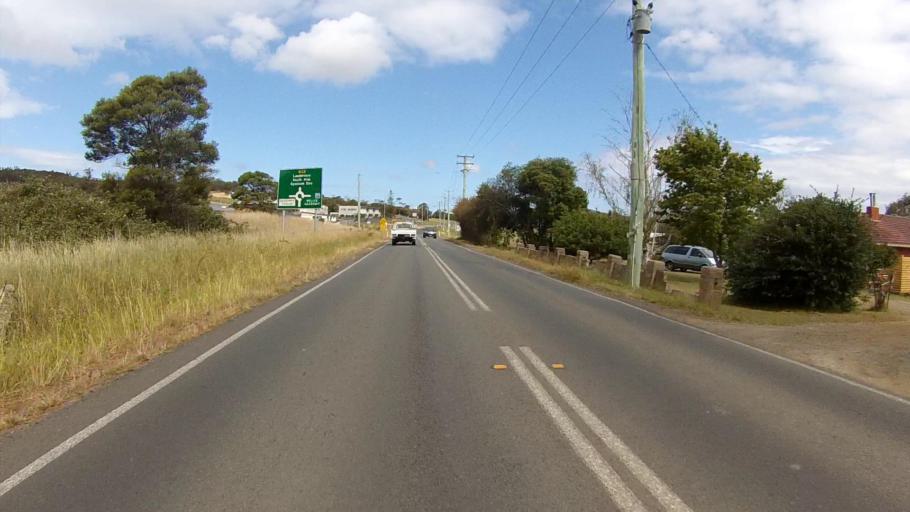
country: AU
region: Tasmania
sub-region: Clarence
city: Rokeby
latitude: -42.9047
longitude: 147.4527
